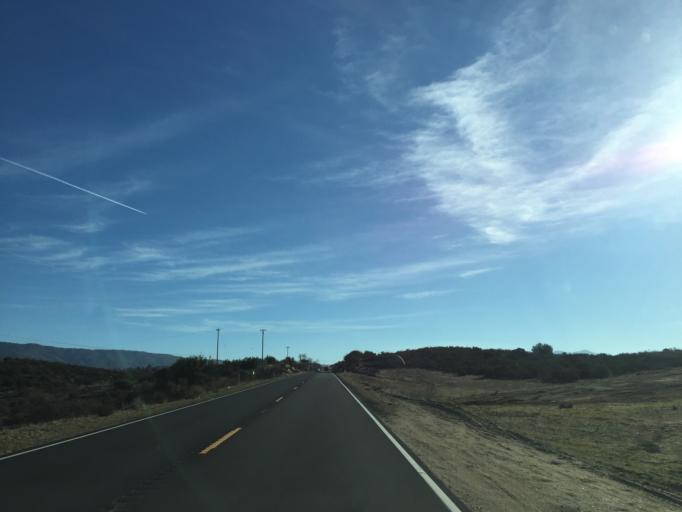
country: US
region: California
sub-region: Riverside County
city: Anza
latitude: 33.5419
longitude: -116.7405
